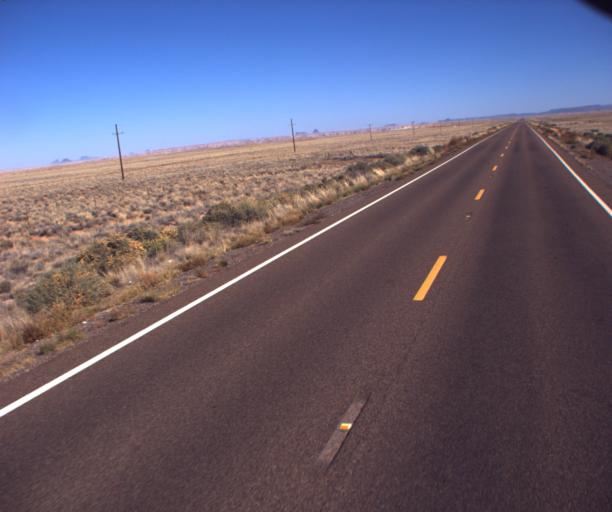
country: US
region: Arizona
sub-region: Navajo County
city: Winslow
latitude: 35.0975
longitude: -110.5381
